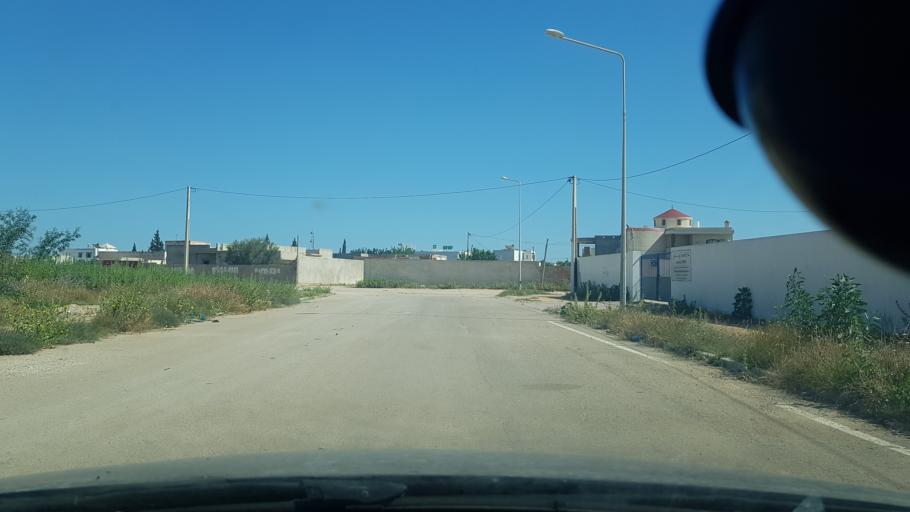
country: TN
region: Safaqis
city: Al Qarmadah
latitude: 34.8326
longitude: 10.7619
